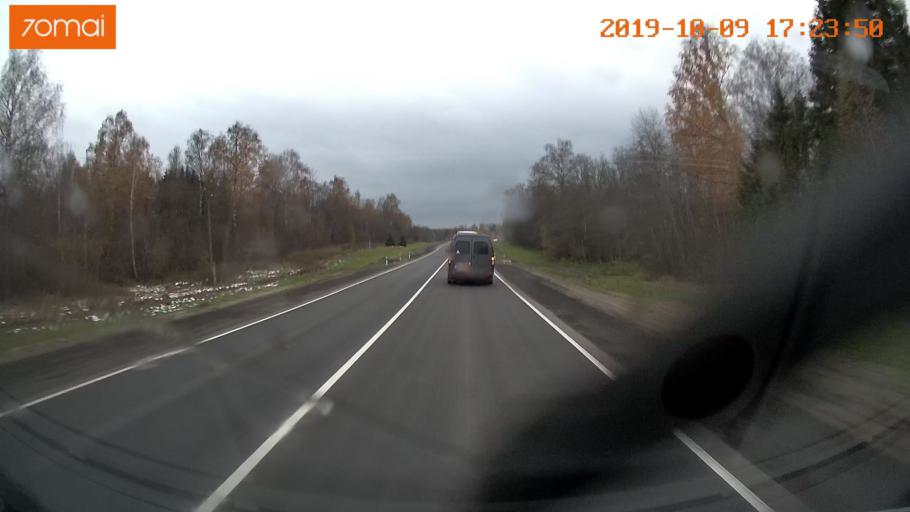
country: RU
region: Ivanovo
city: Furmanov
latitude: 57.1909
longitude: 41.1133
